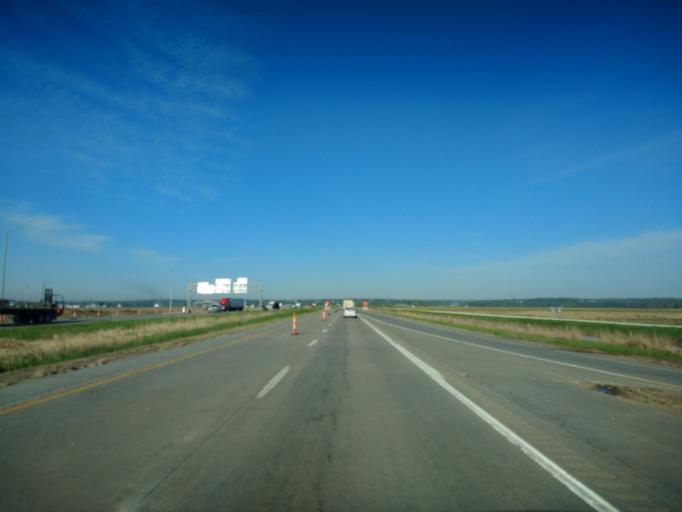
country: US
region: Iowa
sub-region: Pottawattamie County
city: Carter Lake
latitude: 41.3533
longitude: -95.9049
